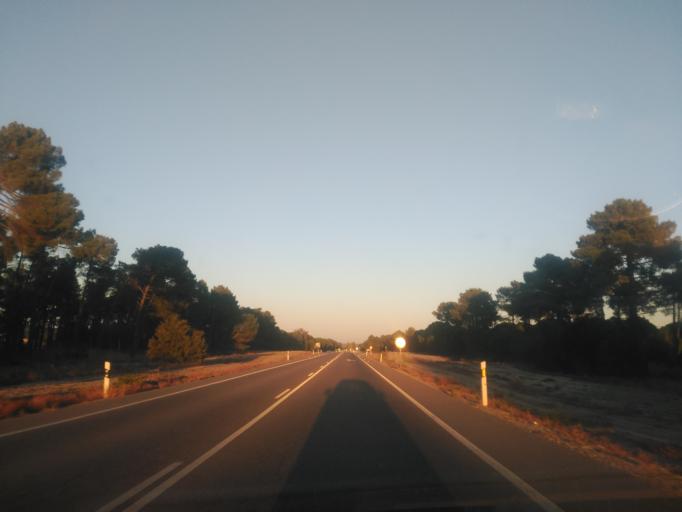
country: ES
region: Castille and Leon
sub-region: Provincia de Valladolid
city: Traspinedo
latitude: 41.5998
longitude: -4.4887
